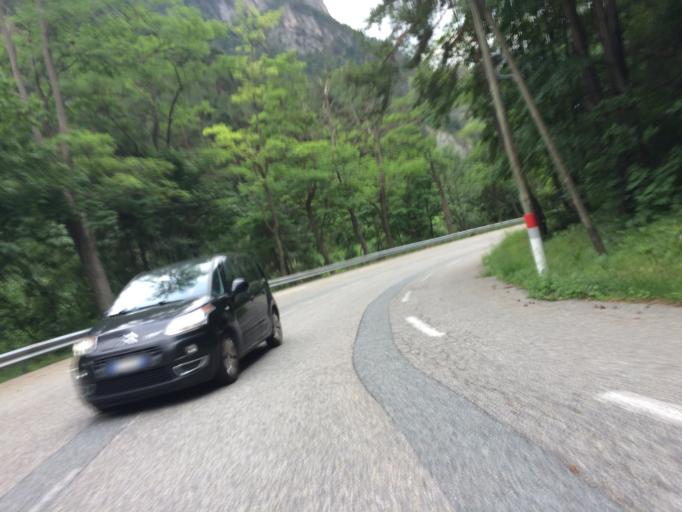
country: FR
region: Provence-Alpes-Cote d'Azur
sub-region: Departement des Alpes-Maritimes
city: Tende
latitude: 44.1283
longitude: 7.5673
